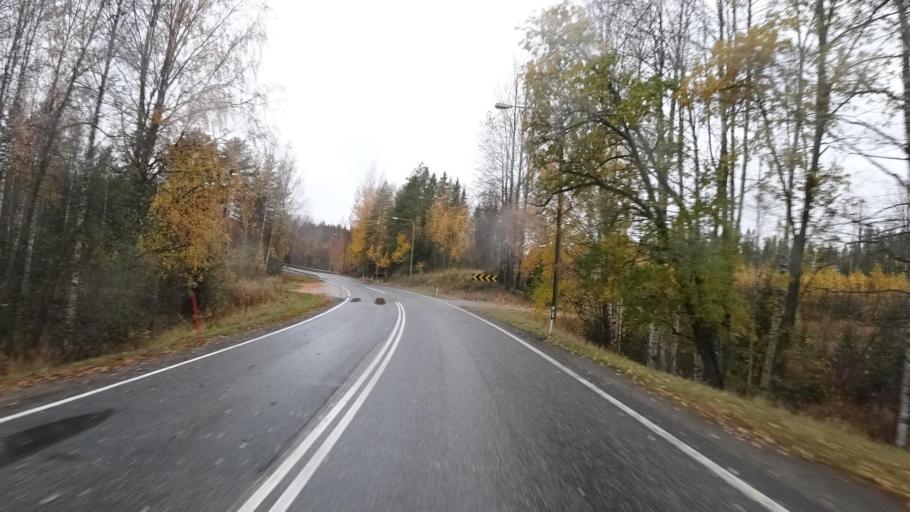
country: FI
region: Northern Savo
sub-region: Koillis-Savo
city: Tuusniemi
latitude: 62.7972
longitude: 28.5391
